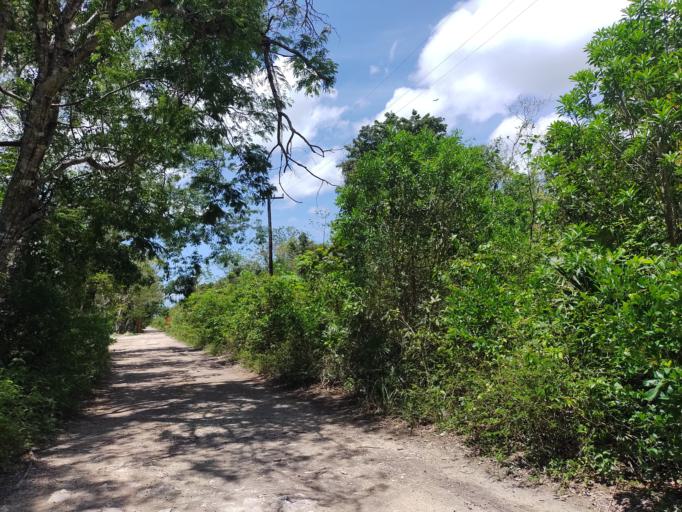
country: MX
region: Quintana Roo
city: San Miguel de Cozumel
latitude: 20.4958
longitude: -86.9038
